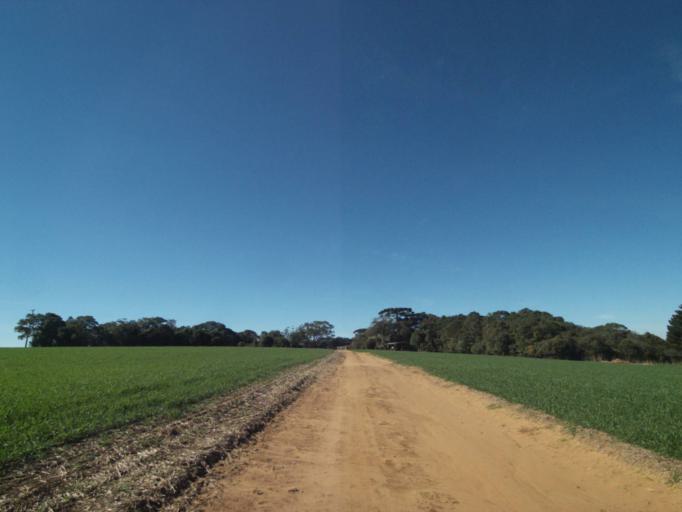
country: BR
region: Parana
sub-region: Tibagi
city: Tibagi
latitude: -24.5989
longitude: -50.2418
